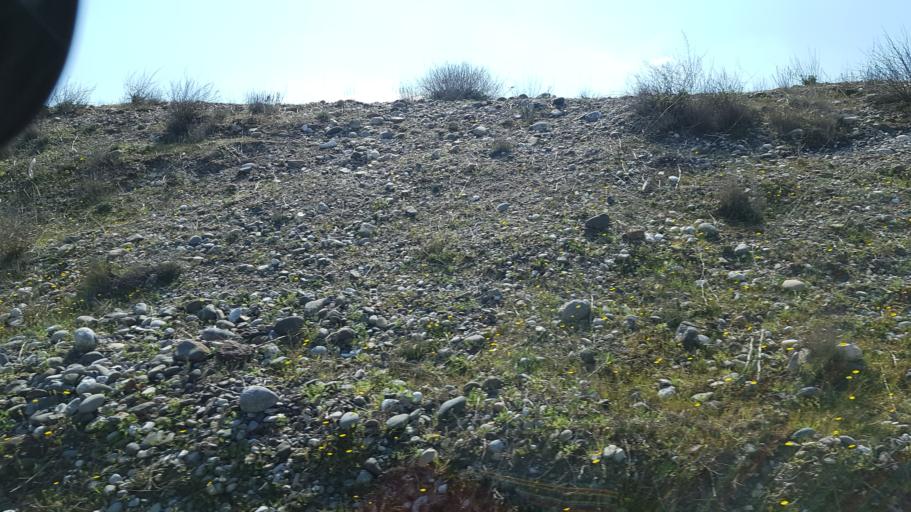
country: AL
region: Shkoder
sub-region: Rrethi i Shkodres
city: Vau i Dejes
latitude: 42.0002
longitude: 19.6066
